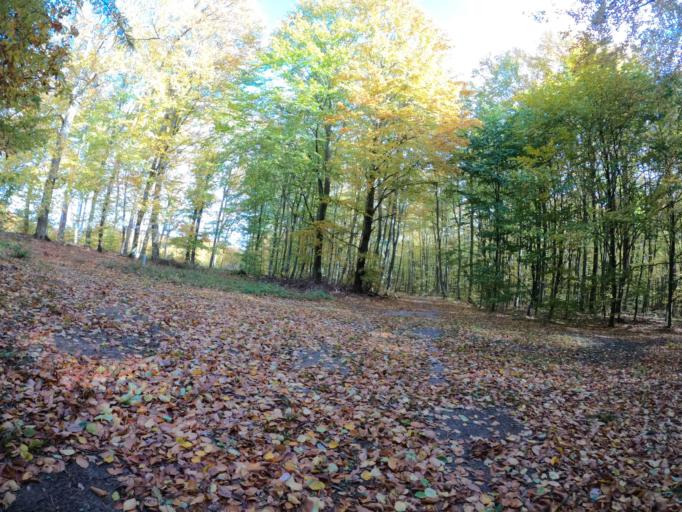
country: PL
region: West Pomeranian Voivodeship
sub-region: Powiat mysliborski
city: Barlinek
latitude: 52.9699
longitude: 15.2311
